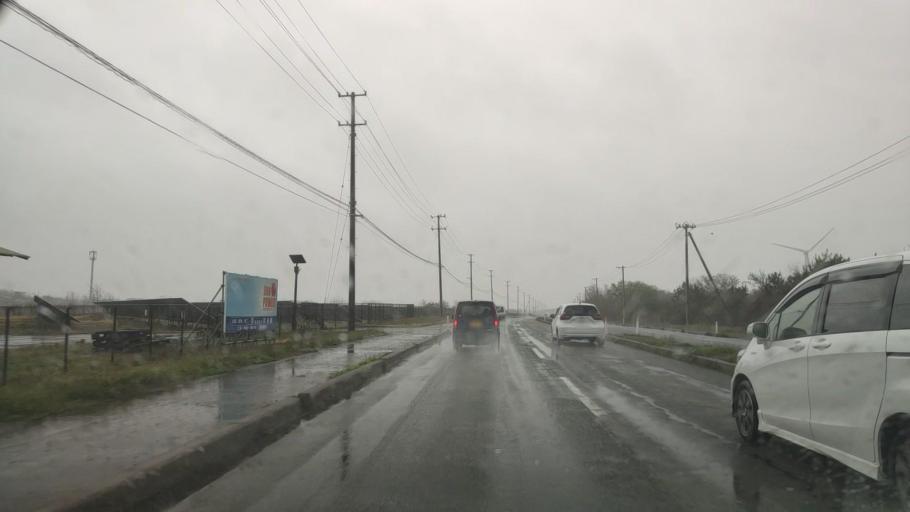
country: JP
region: Akita
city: Tenno
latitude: 39.8915
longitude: 139.9605
